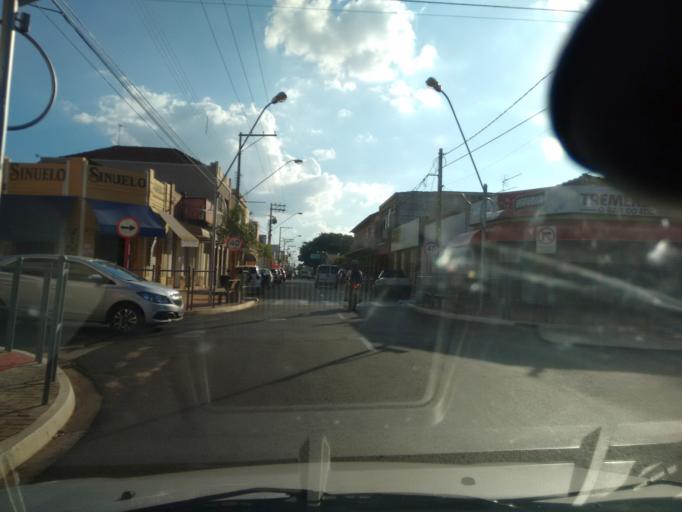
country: BR
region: Sao Paulo
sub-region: Araraquara
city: Araraquara
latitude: -21.7998
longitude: -48.1824
